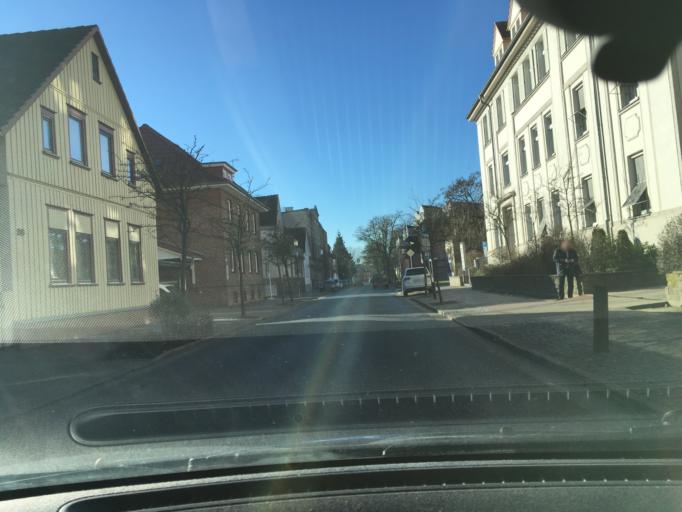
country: DE
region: Lower Saxony
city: Uelzen
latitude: 52.9712
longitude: 10.5573
